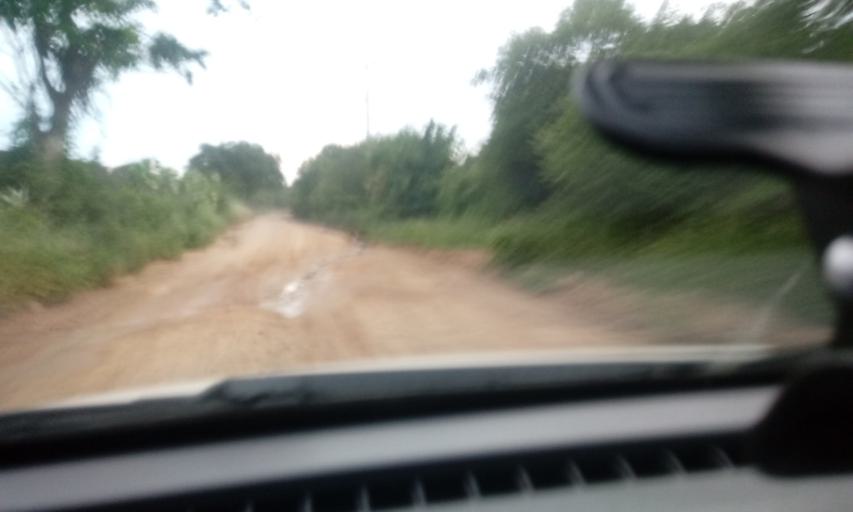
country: BR
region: Bahia
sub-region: Riacho De Santana
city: Riacho de Santana
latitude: -13.8037
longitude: -42.7543
